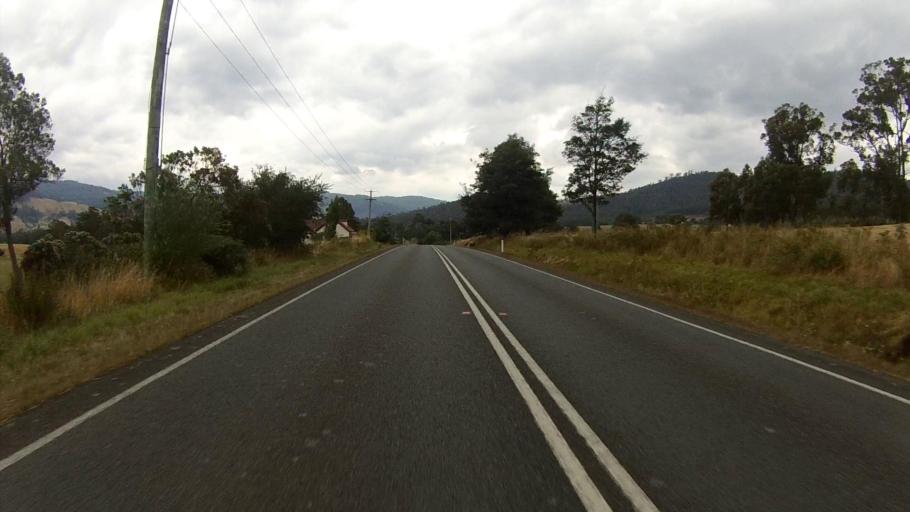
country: AU
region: Tasmania
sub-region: Huon Valley
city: Franklin
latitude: -43.1108
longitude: 147.0360
